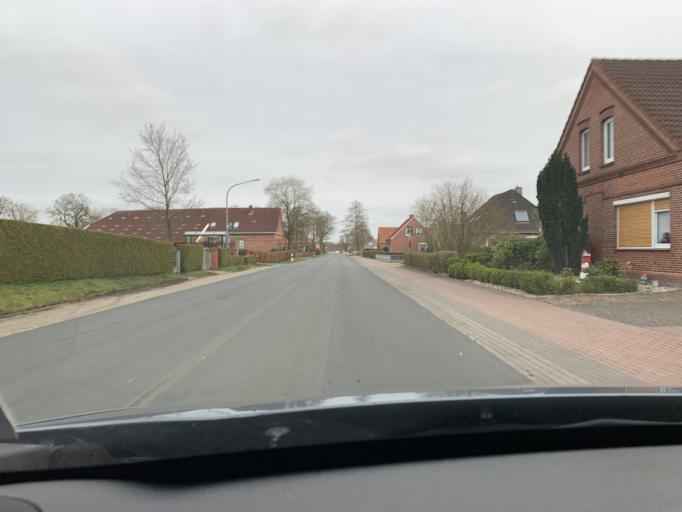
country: DE
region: Lower Saxony
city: Detern
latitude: 53.2443
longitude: 7.7324
